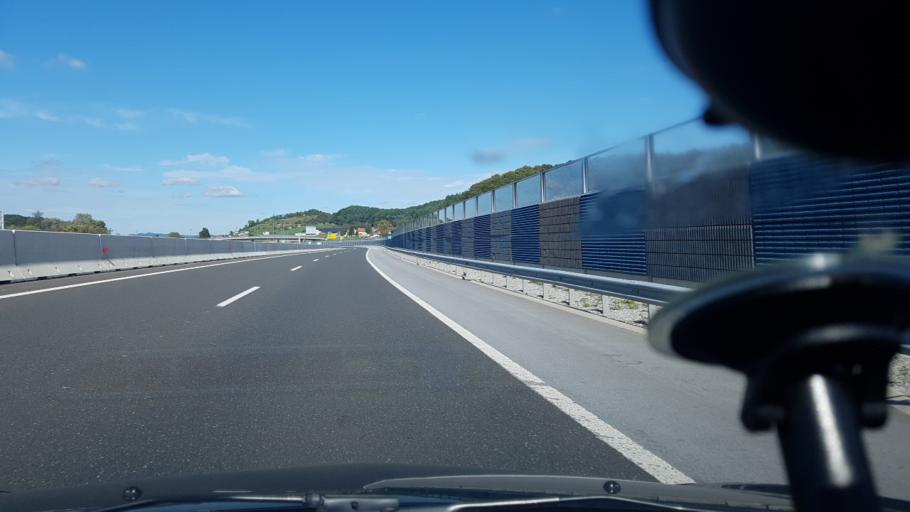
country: SI
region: Podlehnik
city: Podlehnik
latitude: 46.3347
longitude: 15.8770
